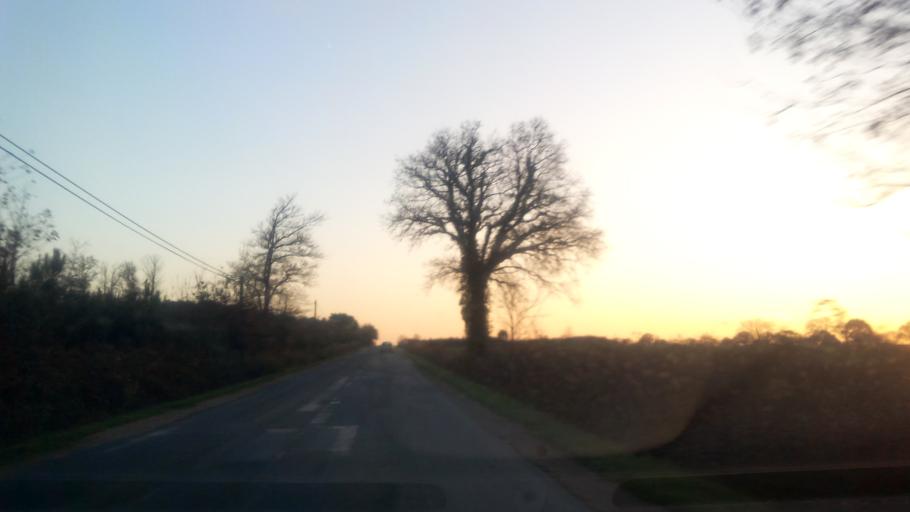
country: FR
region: Brittany
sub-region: Departement d'Ille-et-Vilaine
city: Bains-sur-Oust
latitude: 47.7258
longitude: -2.0526
